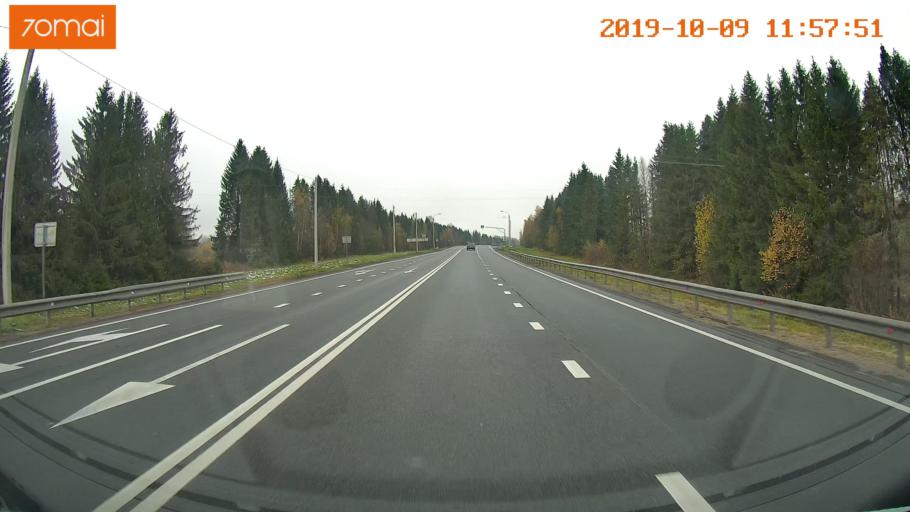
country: RU
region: Vologda
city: Gryazovets
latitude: 58.7263
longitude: 40.2950
